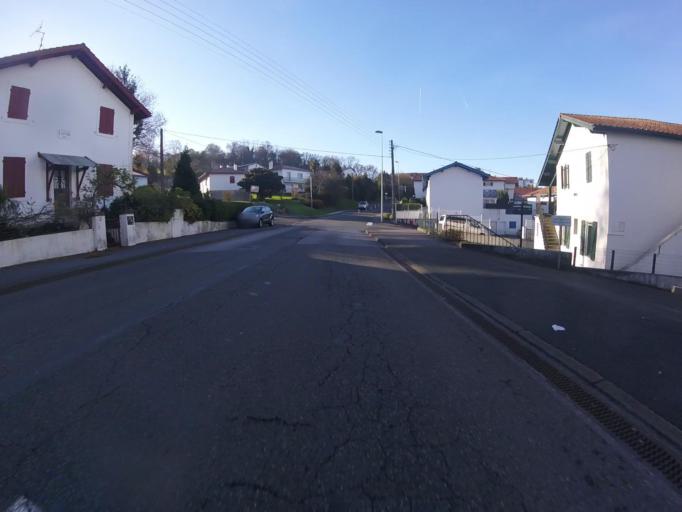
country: FR
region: Aquitaine
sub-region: Departement des Pyrenees-Atlantiques
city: Hendaye
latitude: 43.3566
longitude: -1.7660
